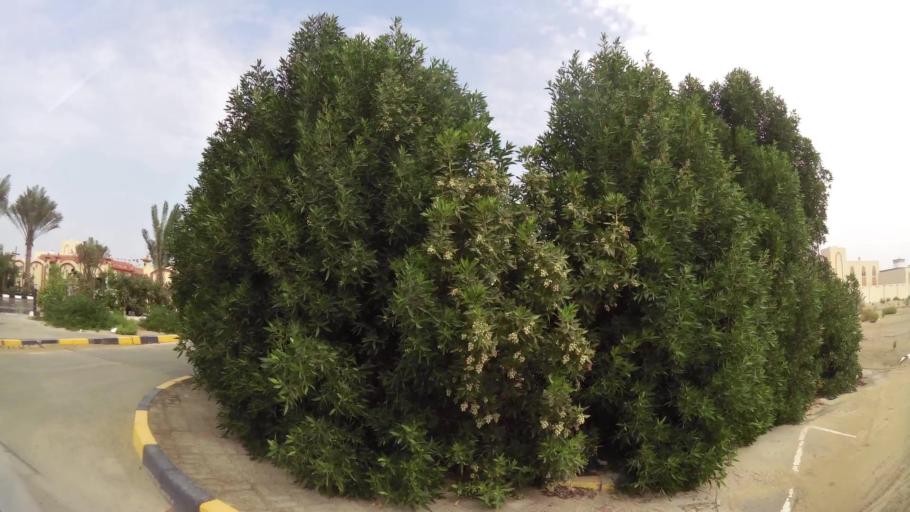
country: AE
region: Abu Dhabi
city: Abu Dhabi
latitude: 24.6319
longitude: 54.6822
